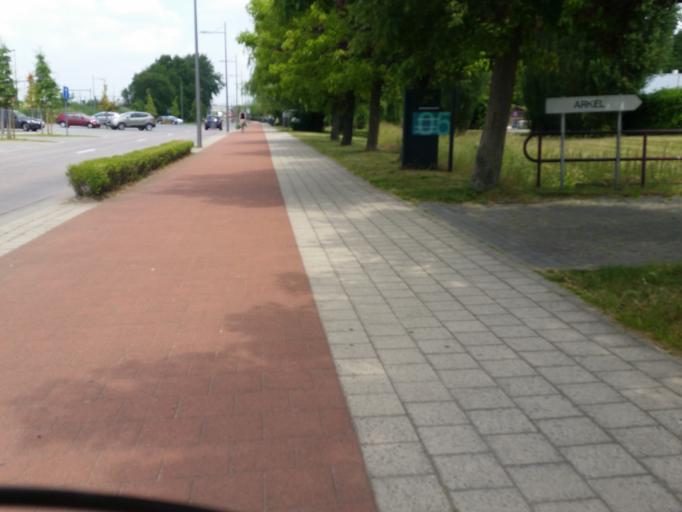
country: BE
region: Flanders
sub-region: Provincie Antwerpen
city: Duffel
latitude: 51.0925
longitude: 4.4937
